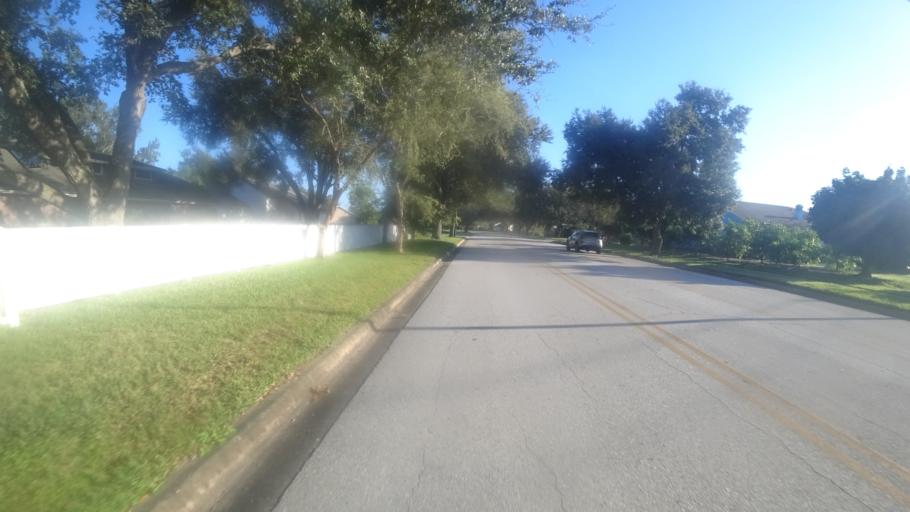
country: US
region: Florida
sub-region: Manatee County
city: Ellenton
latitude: 27.4913
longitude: -82.5015
